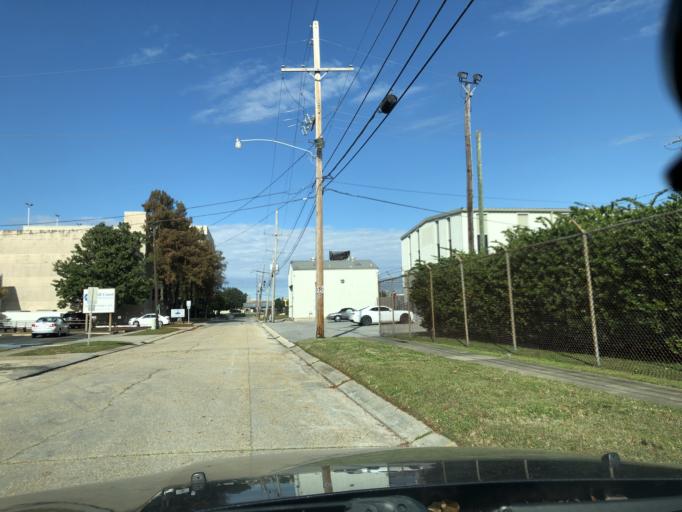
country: US
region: Louisiana
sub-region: Jefferson Parish
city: Metairie
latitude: 29.9955
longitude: -90.1625
